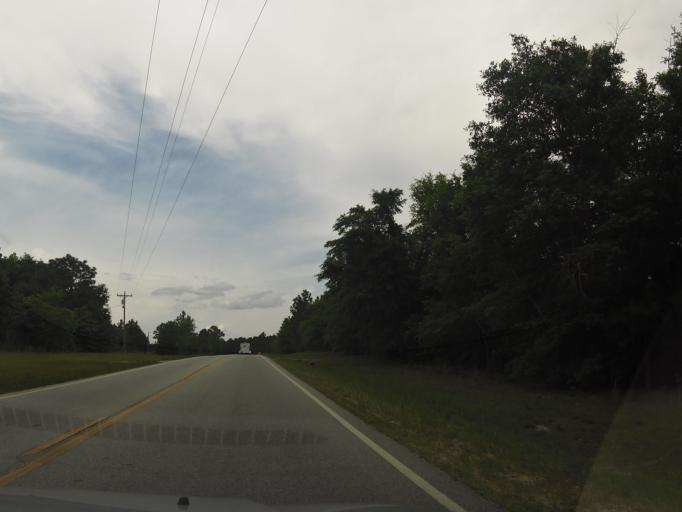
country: US
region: Georgia
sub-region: Emanuel County
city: Swainsboro
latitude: 32.5081
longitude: -82.2612
